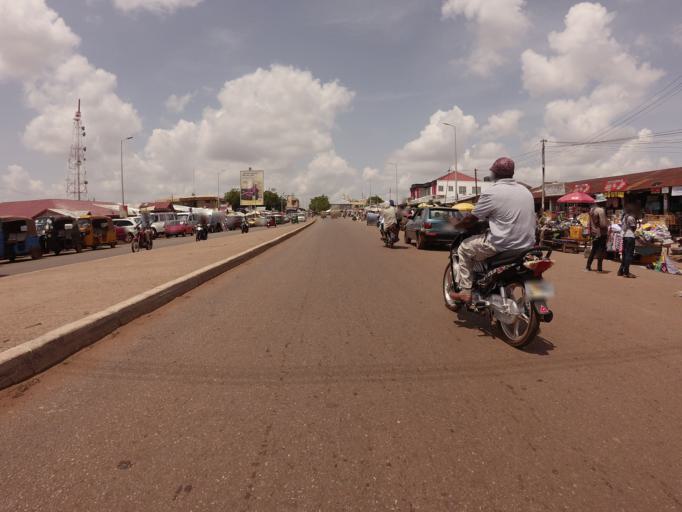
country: GH
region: Northern
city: Tamale
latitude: 9.4043
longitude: -0.8456
